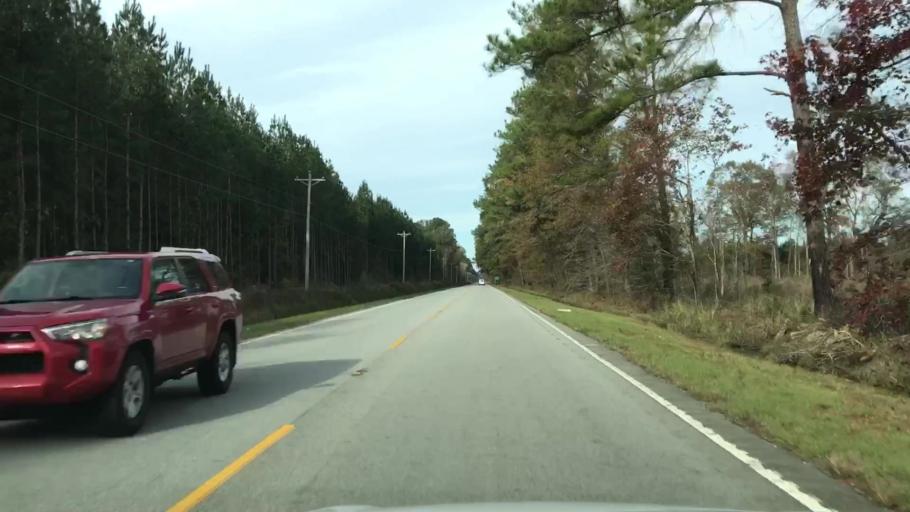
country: US
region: South Carolina
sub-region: Colleton County
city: Walterboro
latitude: 32.8085
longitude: -80.5212
